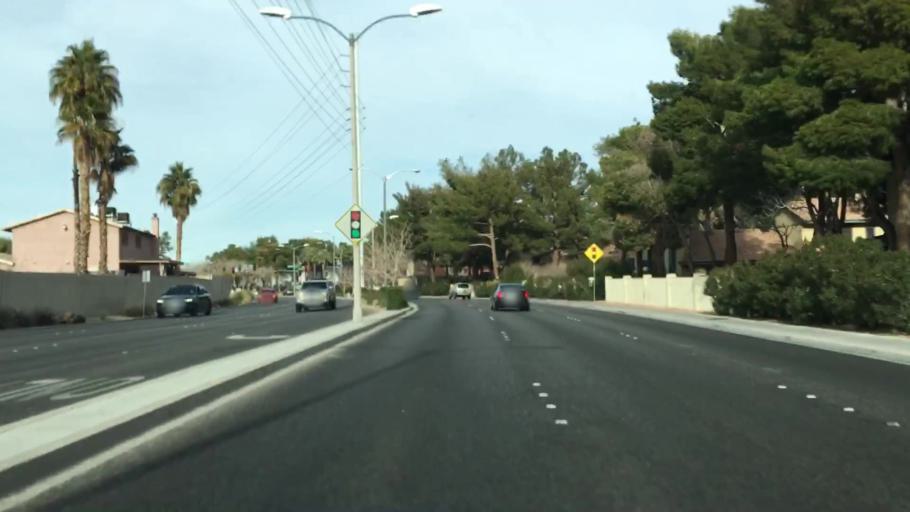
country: US
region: Nevada
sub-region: Clark County
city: Whitney
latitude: 36.0653
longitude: -115.0829
